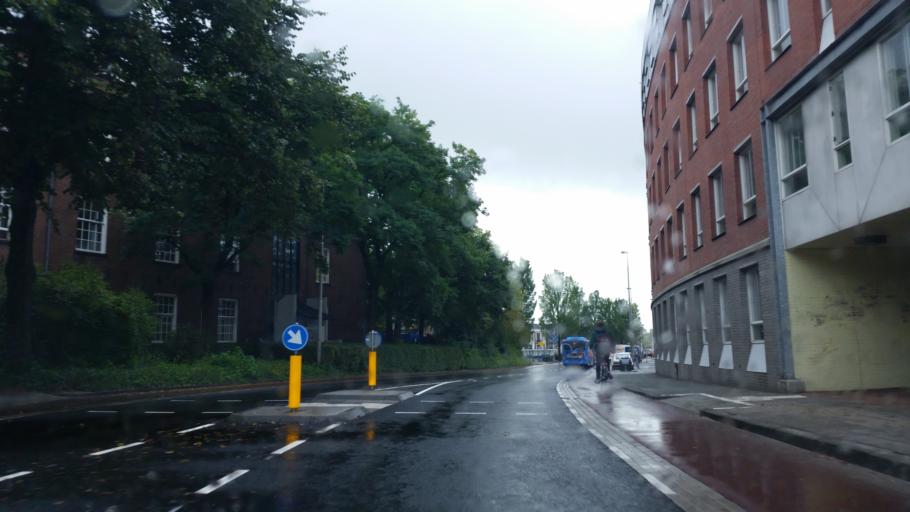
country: NL
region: Friesland
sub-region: Gemeente Leeuwarden
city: Leeuwarden
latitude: 53.2047
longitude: 5.8033
